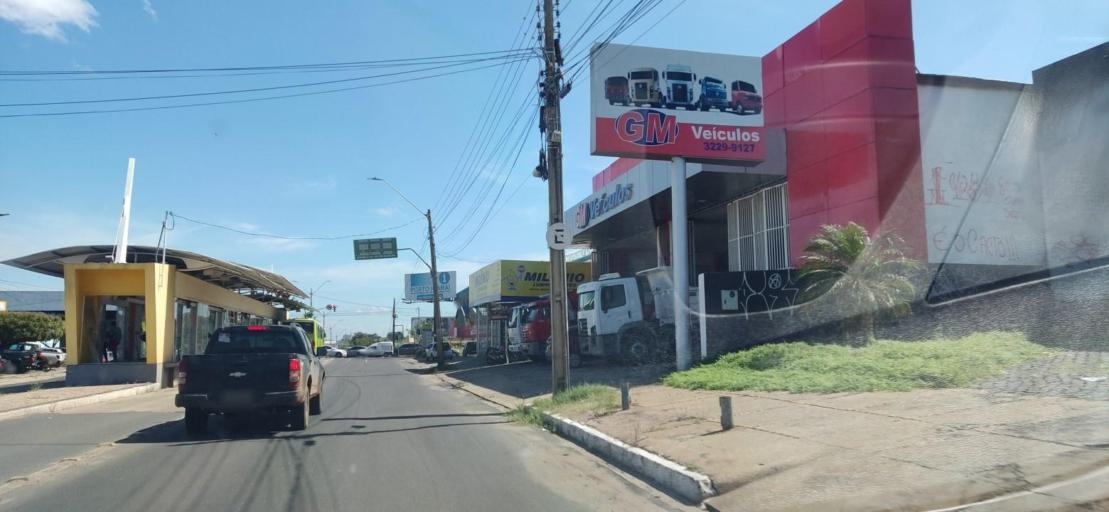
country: BR
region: Piaui
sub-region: Teresina
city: Teresina
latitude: -5.1148
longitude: -42.8051
